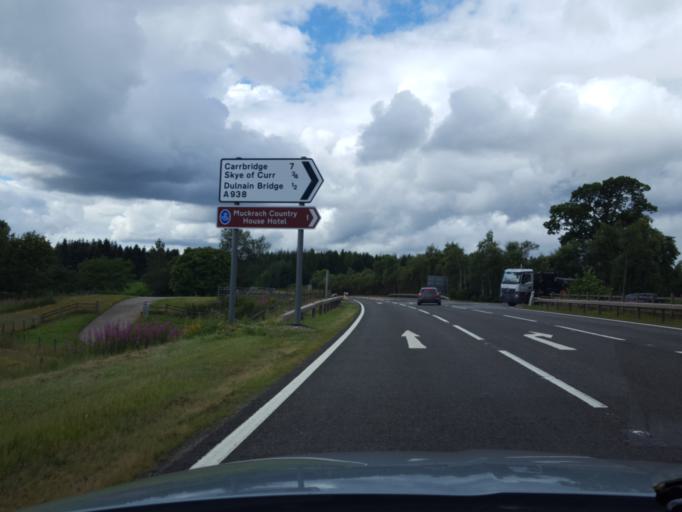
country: GB
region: Scotland
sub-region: Highland
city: Grantown on Spey
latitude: 57.3048
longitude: -3.6540
